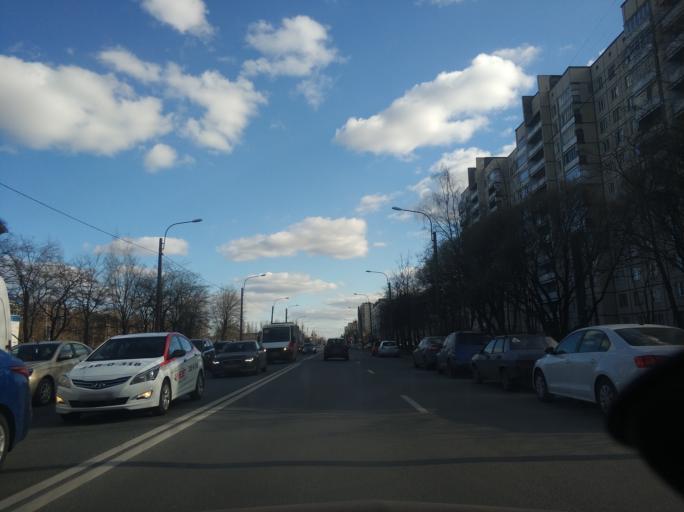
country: RU
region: St.-Petersburg
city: Krasnogvargeisky
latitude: 59.9589
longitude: 30.4918
